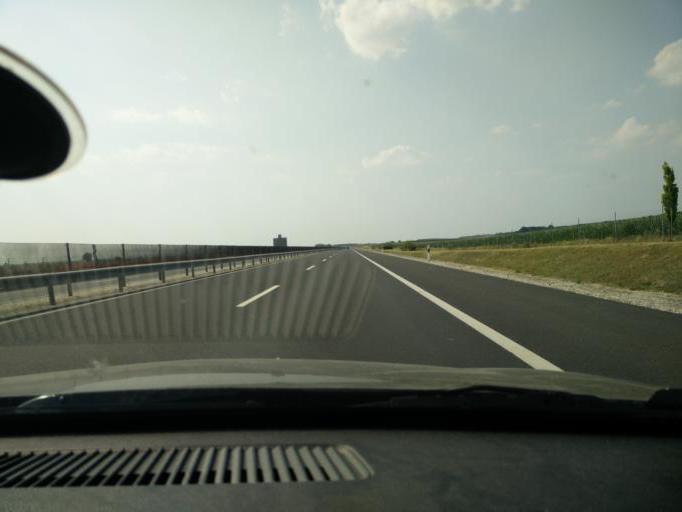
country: HU
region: Tolna
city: Tolna
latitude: 46.4207
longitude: 18.7277
